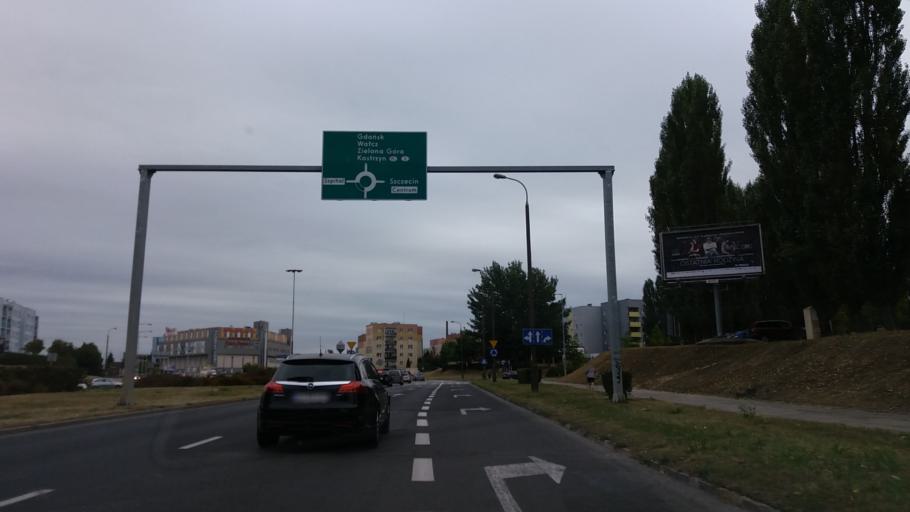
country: PL
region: Lubusz
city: Gorzow Wielkopolski
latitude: 52.7580
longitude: 15.2450
